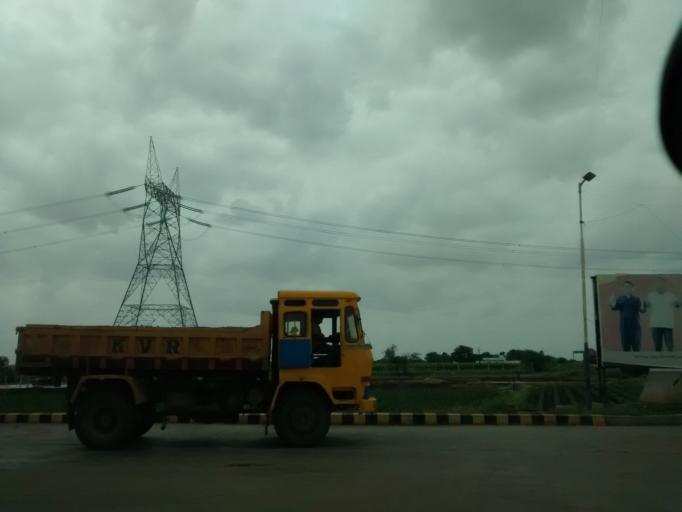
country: IN
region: Telangana
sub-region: Mahbubnagar
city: Alampur
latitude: 15.7229
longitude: 78.0009
